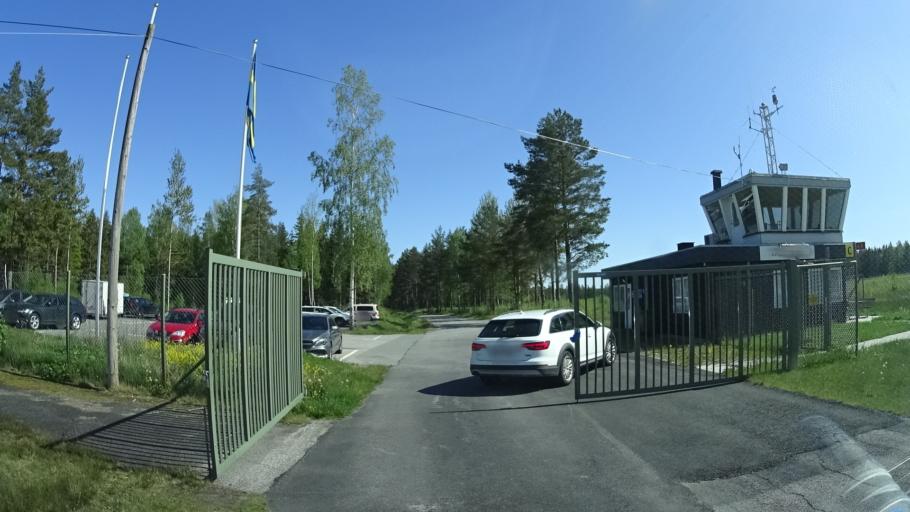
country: SE
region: Kalmar
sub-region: Vasterviks Kommun
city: Vaestervik
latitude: 57.7773
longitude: 16.5292
